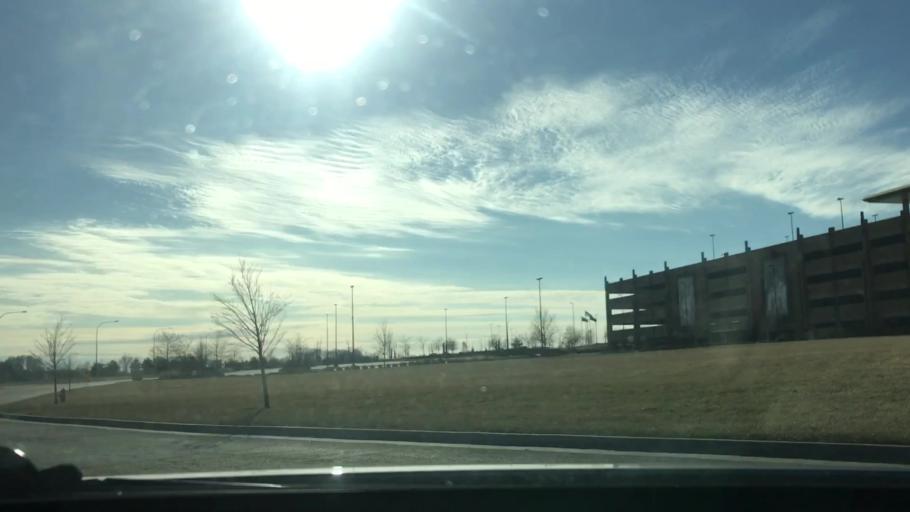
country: US
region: Kansas
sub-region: Wyandotte County
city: Edwardsville
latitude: 39.1129
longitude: -94.8236
